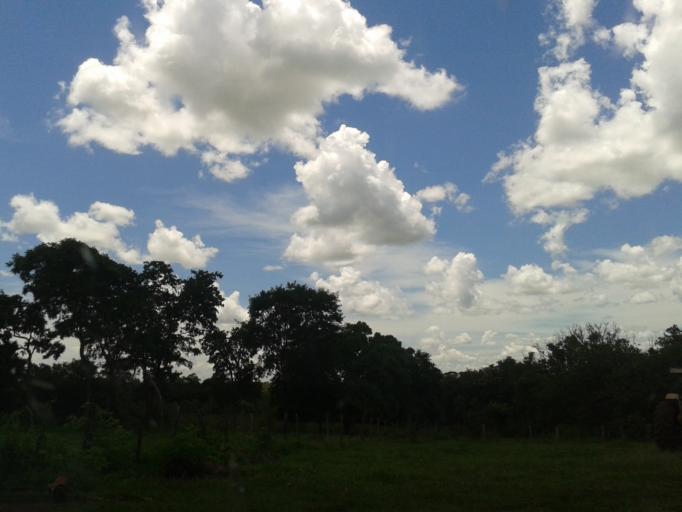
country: BR
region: Minas Gerais
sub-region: Capinopolis
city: Capinopolis
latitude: -18.7786
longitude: -49.8014
